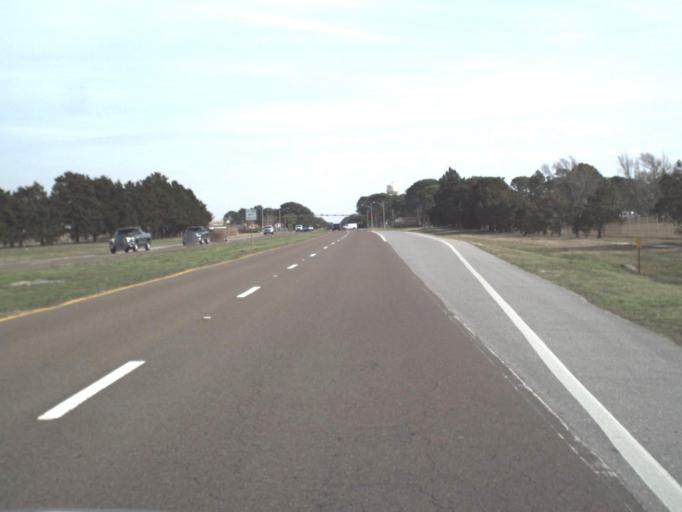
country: US
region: Florida
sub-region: Bay County
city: Tyndall Air Force Base
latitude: 30.0726
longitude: -85.5937
